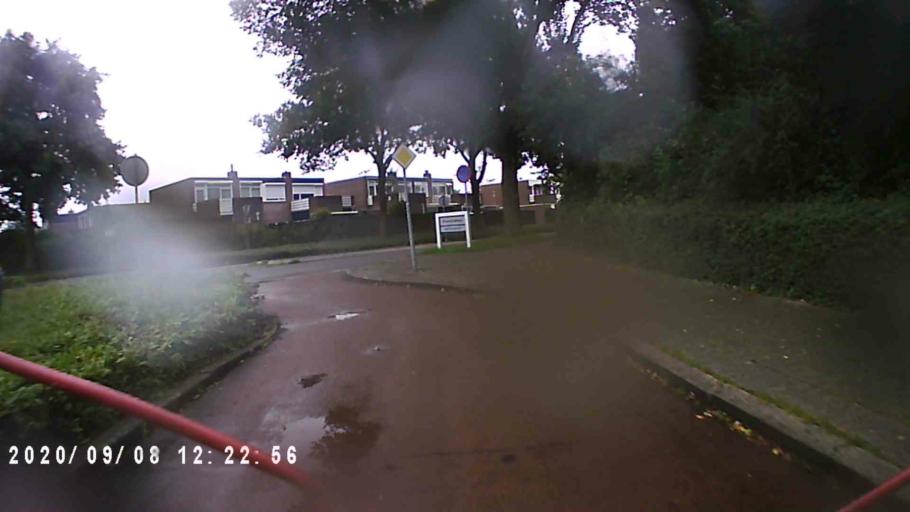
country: NL
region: Groningen
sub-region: Gemeente Veendam
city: Veendam
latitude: 53.0943
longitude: 6.8567
